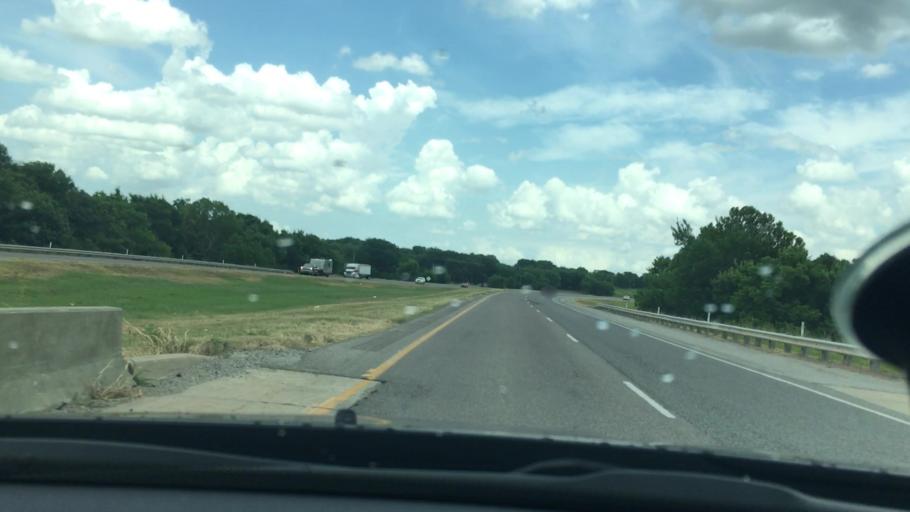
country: US
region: Oklahoma
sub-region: Murray County
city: Sulphur
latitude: 34.5065
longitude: -97.0335
